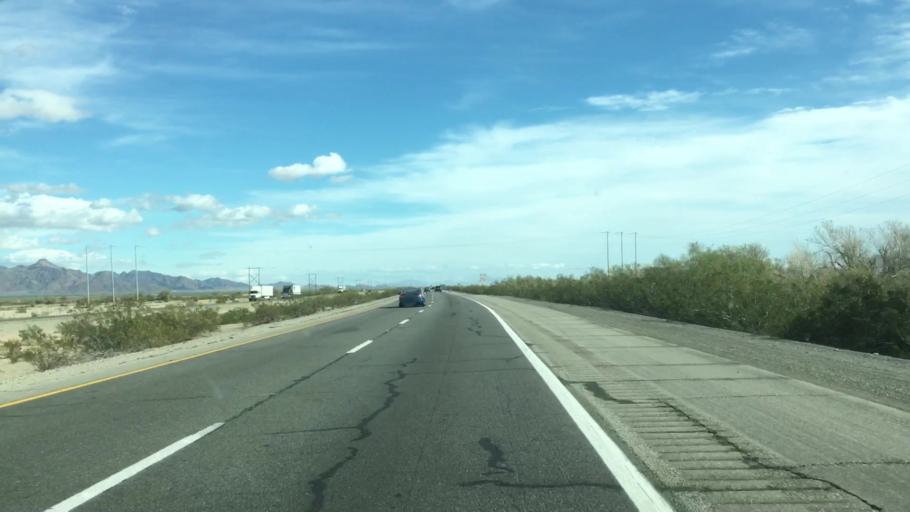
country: US
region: California
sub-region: Riverside County
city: Mesa Verde
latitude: 33.6059
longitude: -114.9811
